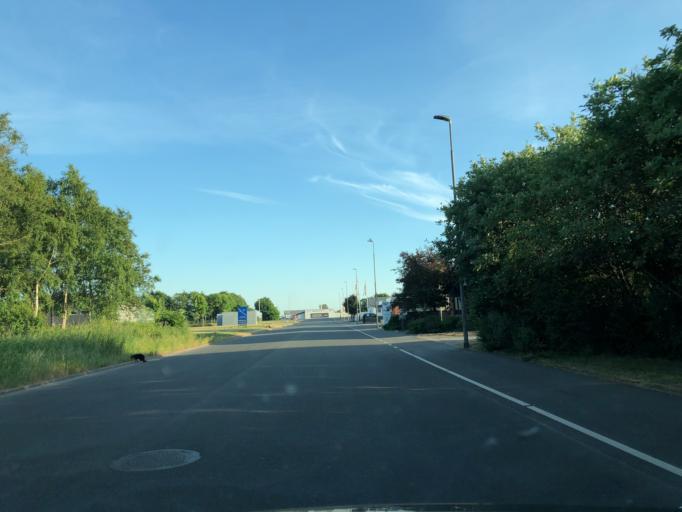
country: DK
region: Central Jutland
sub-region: Struer Kommune
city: Struer
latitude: 56.4825
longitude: 8.5772
